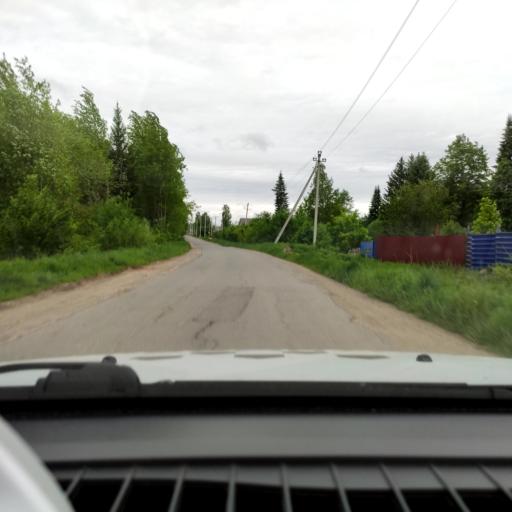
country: RU
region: Perm
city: Novyye Lyady
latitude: 58.0435
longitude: 56.6184
